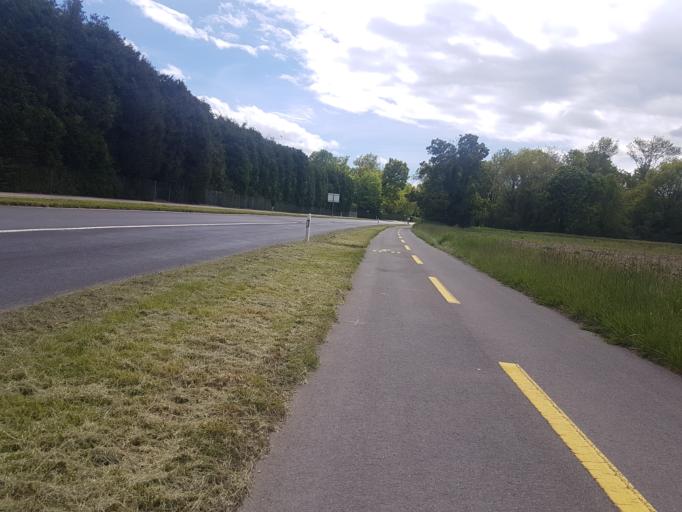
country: CH
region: Vaud
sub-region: Nyon District
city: Founex
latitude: 46.3418
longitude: 6.2052
